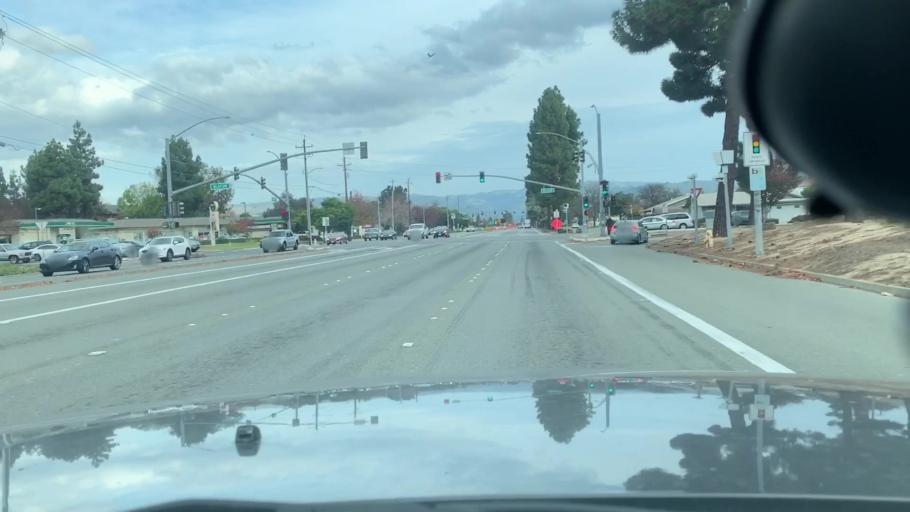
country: US
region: California
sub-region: Alameda County
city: Fremont
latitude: 37.5358
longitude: -121.9987
